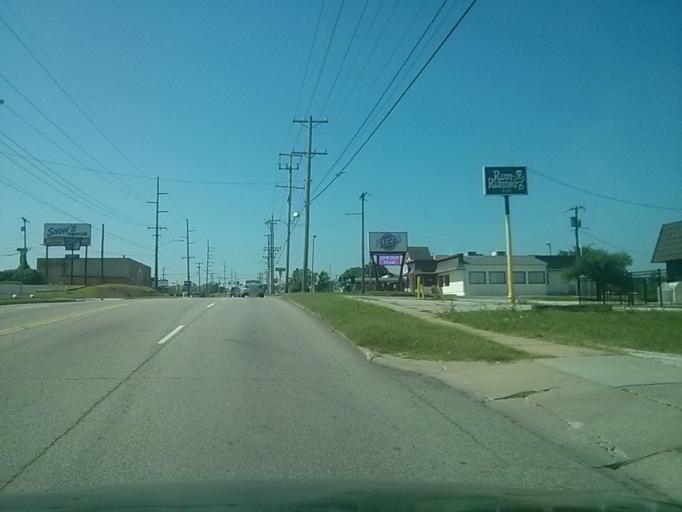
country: US
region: Oklahoma
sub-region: Tulsa County
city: Tulsa
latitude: 36.1503
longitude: -95.9046
